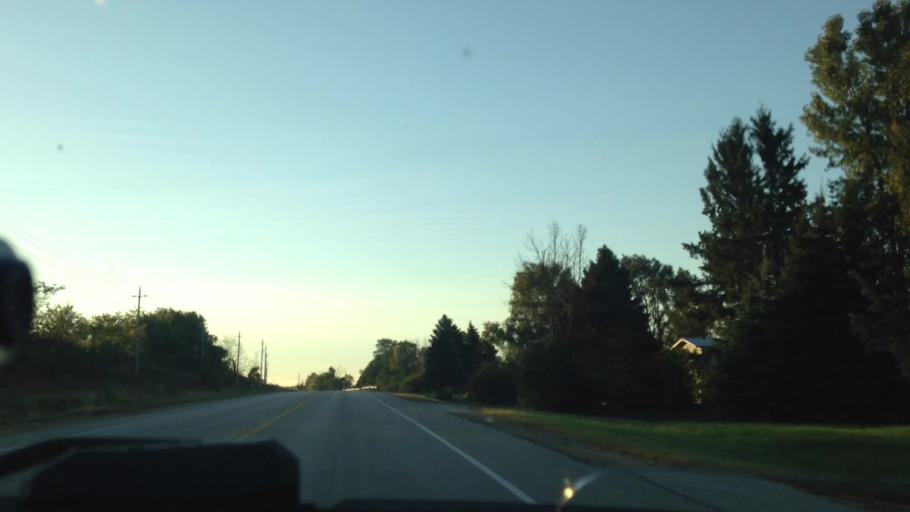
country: US
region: Wisconsin
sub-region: Ozaukee County
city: Saukville
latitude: 43.3935
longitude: -87.9759
